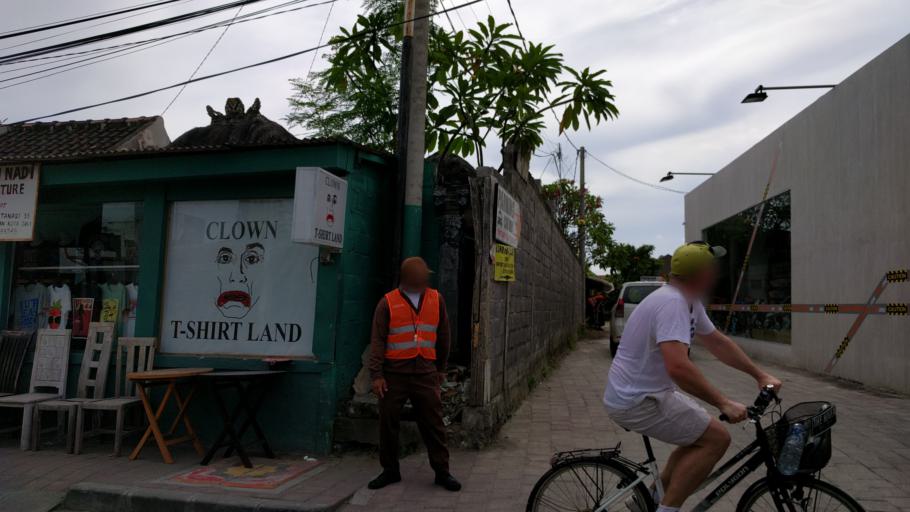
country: ID
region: Bali
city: Kuta
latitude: -8.6796
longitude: 115.1676
